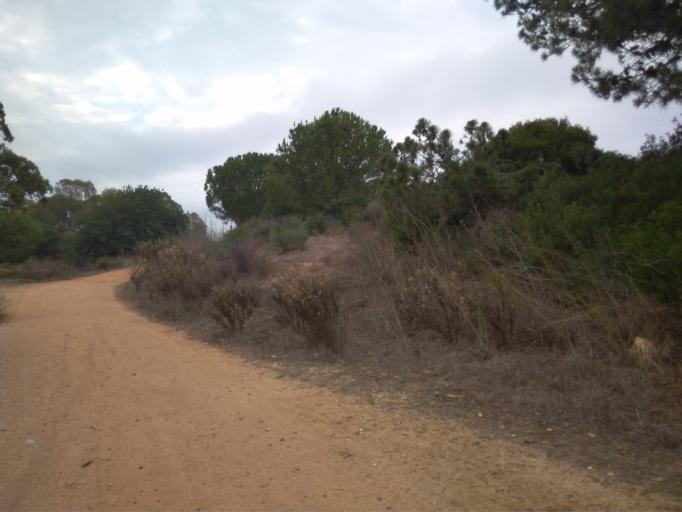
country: PT
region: Faro
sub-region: Loule
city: Almancil
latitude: 37.0260
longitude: -8.0057
